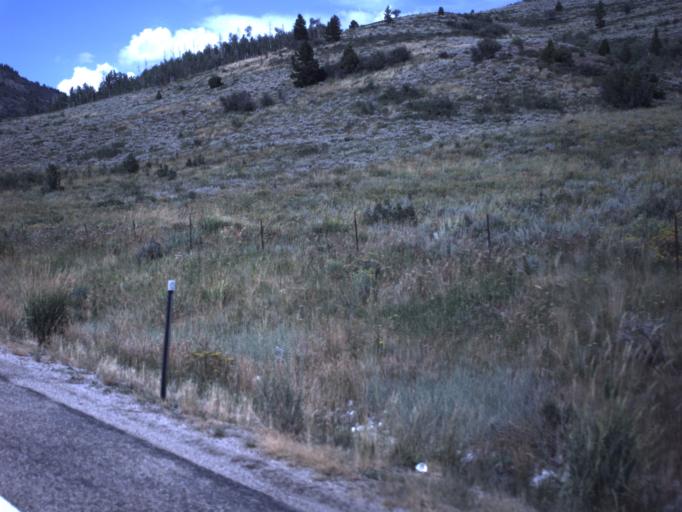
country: US
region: Utah
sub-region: Cache County
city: Richmond
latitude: 41.9272
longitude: -111.5609
